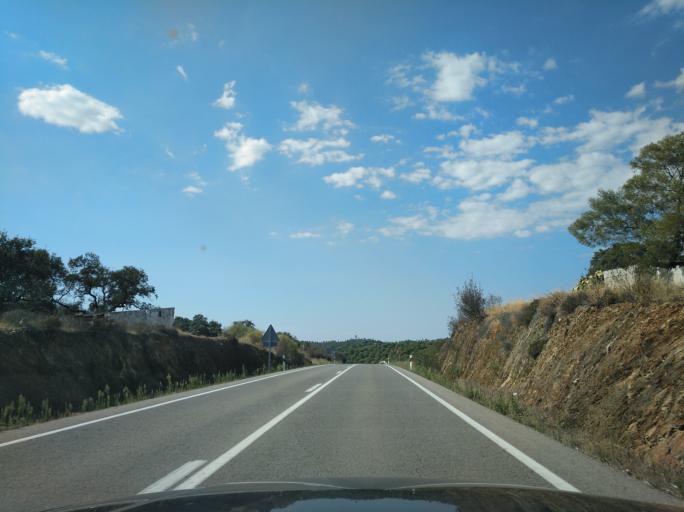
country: ES
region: Andalusia
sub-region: Provincia de Huelva
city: Santa Barbara de Casa
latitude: 37.7991
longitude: -7.1978
